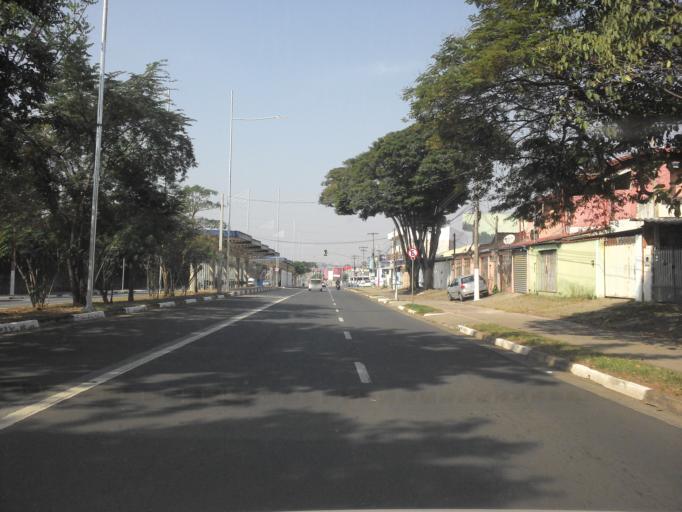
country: BR
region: Sao Paulo
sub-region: Hortolandia
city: Hortolandia
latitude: -22.8771
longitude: -47.2004
